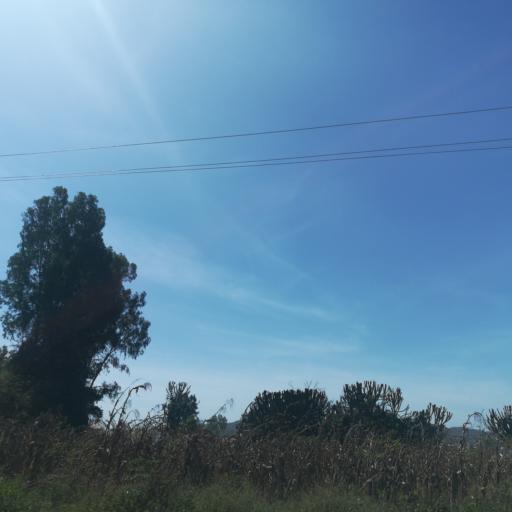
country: NG
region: Plateau
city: Bukuru
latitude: 9.7585
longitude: 8.8652
